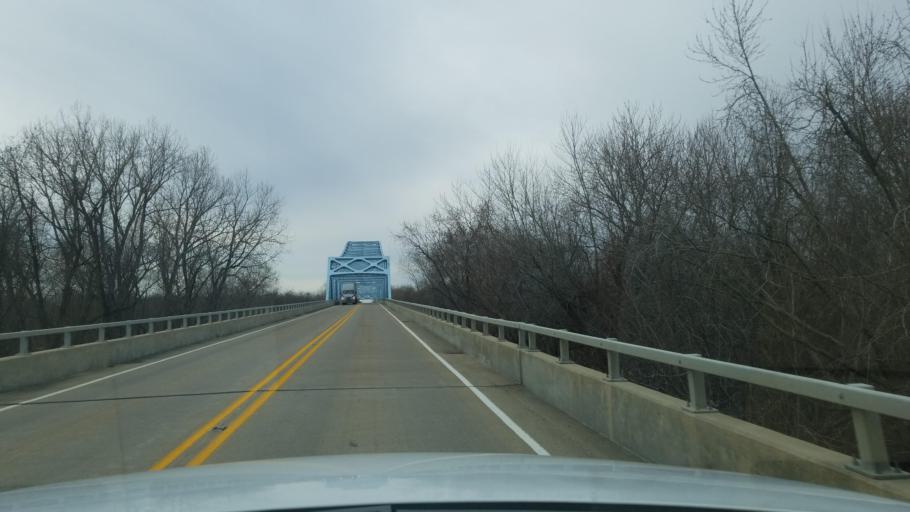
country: US
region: Indiana
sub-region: Posey County
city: Mount Vernon
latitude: 37.9440
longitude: -88.0329
